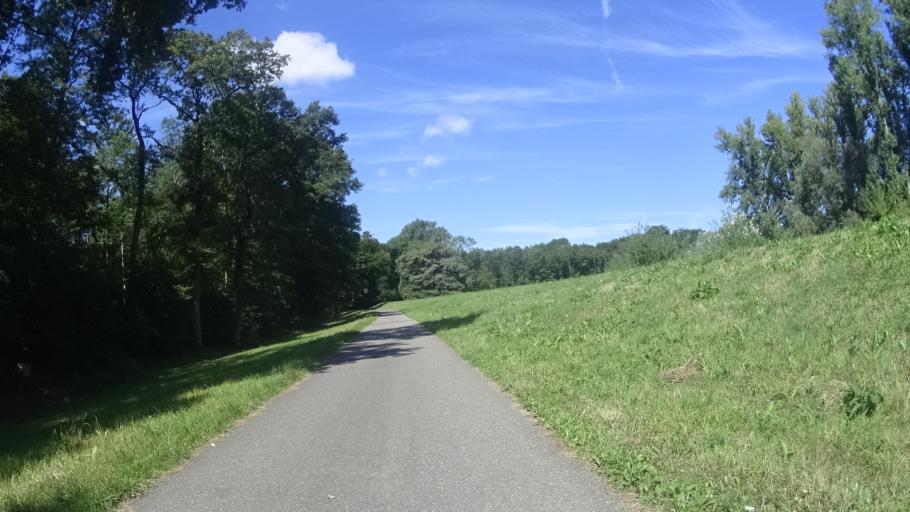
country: DE
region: Rheinland-Pfalz
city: Leimersheim
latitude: 49.1562
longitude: 8.3621
